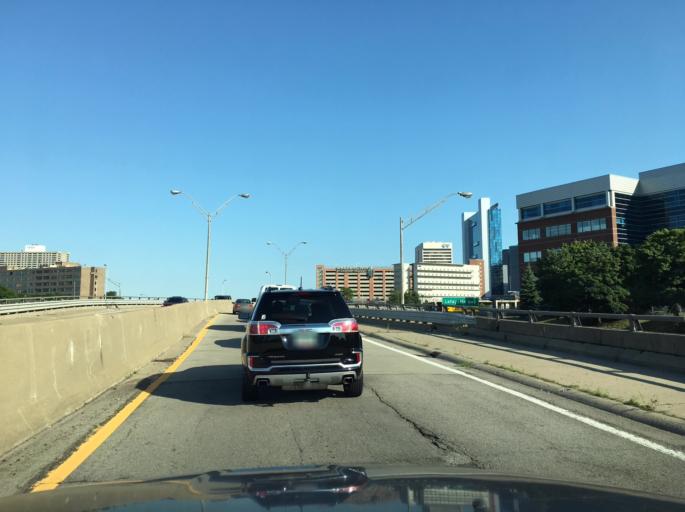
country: US
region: Michigan
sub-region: Wayne County
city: Detroit
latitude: 42.3409
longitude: -83.0427
